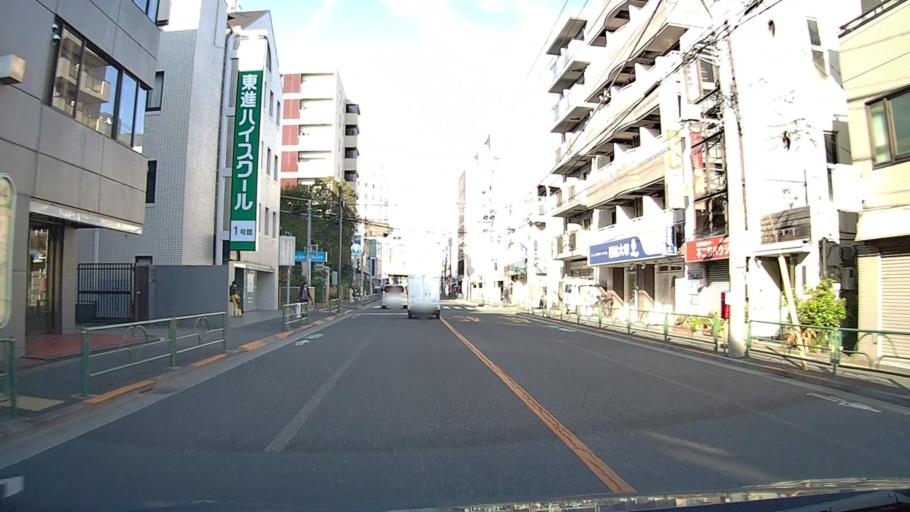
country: JP
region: Tokyo
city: Musashino
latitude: 35.7012
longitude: 139.5824
